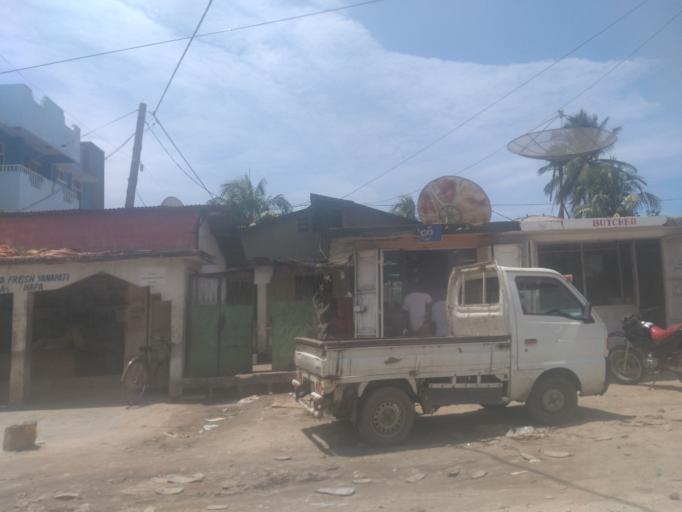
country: TZ
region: Zanzibar Urban/West
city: Zanzibar
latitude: -6.2065
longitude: 39.2148
